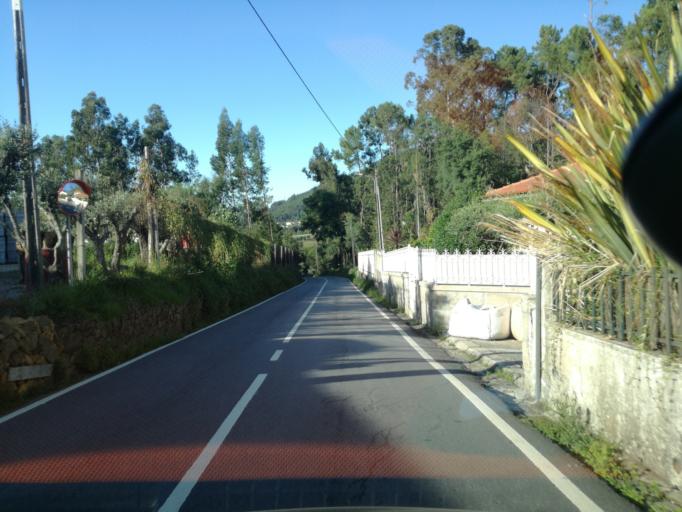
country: PT
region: Porto
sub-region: Santo Tirso
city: Sao Miguel do Couto
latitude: 41.3090
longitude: -8.4614
